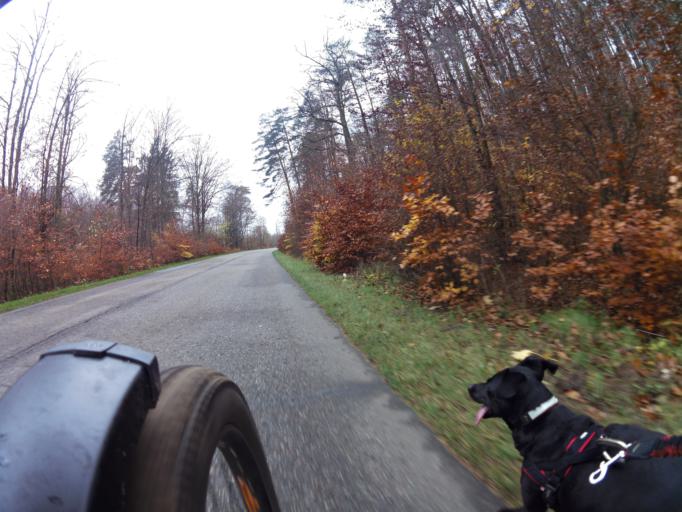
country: PL
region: Pomeranian Voivodeship
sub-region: Powiat wejherowski
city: Orle
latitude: 54.7027
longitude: 18.1485
